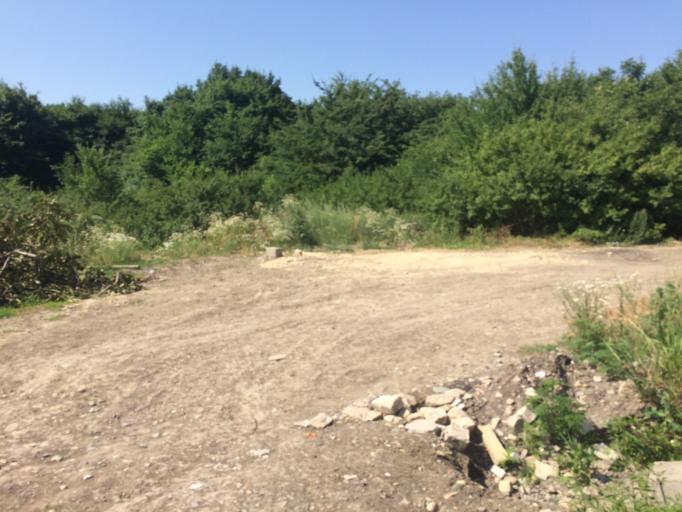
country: RU
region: Stavropol'skiy
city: Tatarka
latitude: 44.9802
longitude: 41.9406
